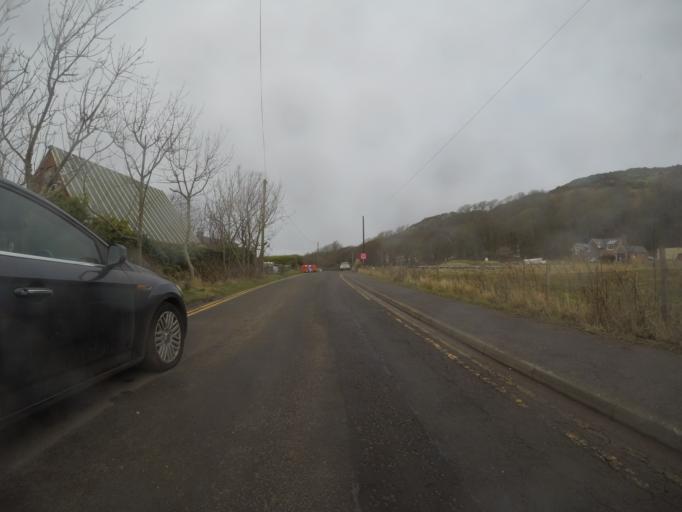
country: GB
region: Scotland
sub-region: North Ayrshire
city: West Kilbride
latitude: 55.6996
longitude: -4.9037
